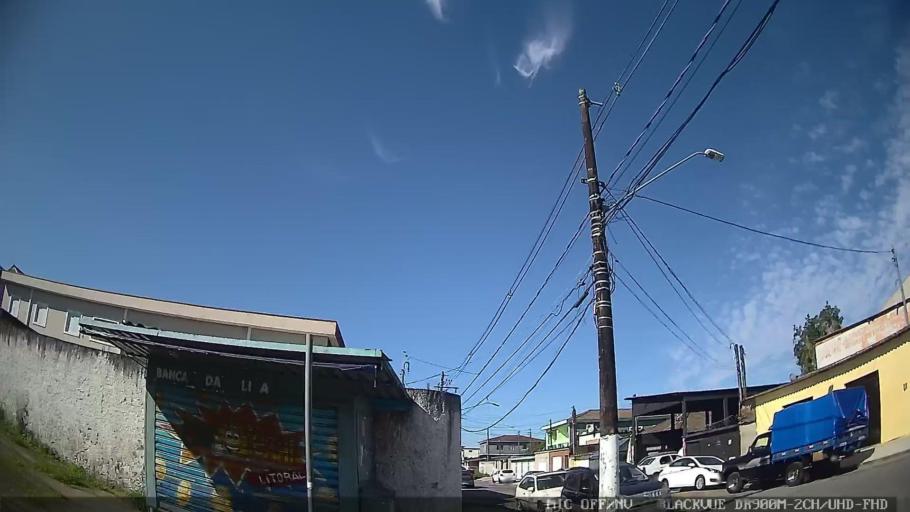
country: BR
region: Sao Paulo
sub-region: Santos
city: Santos
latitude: -23.9551
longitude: -46.2877
